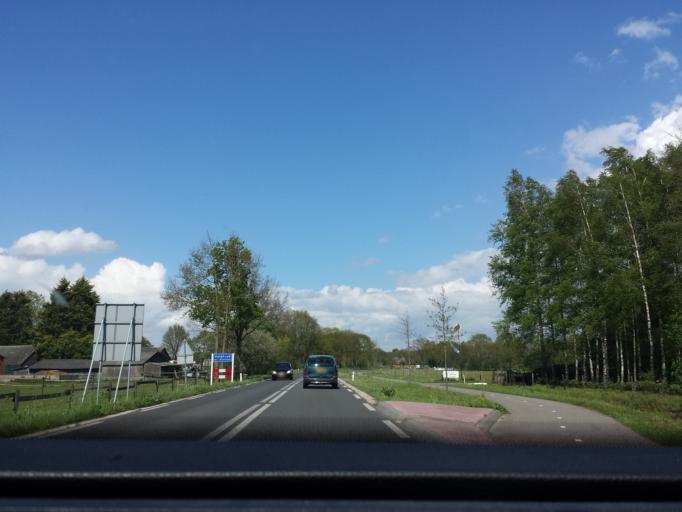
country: NL
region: Gelderland
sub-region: Gemeente Bronckhorst
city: Zelhem
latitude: 52.0477
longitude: 6.4134
